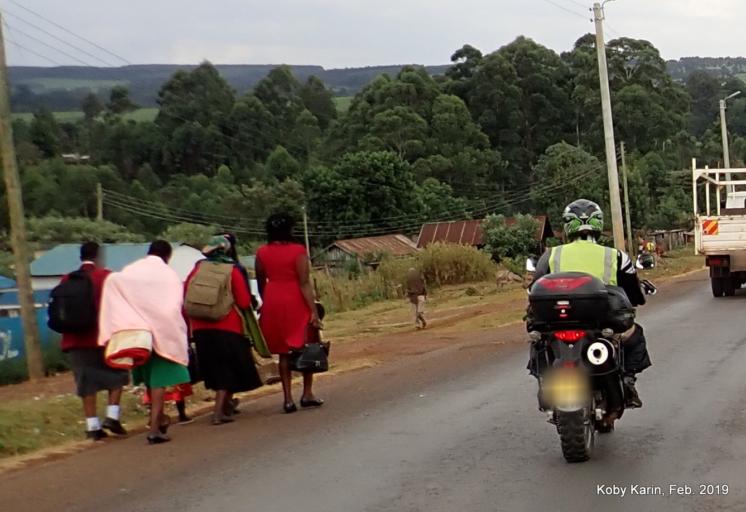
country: KE
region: Kericho
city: Kericho
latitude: -0.3795
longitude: 35.2526
